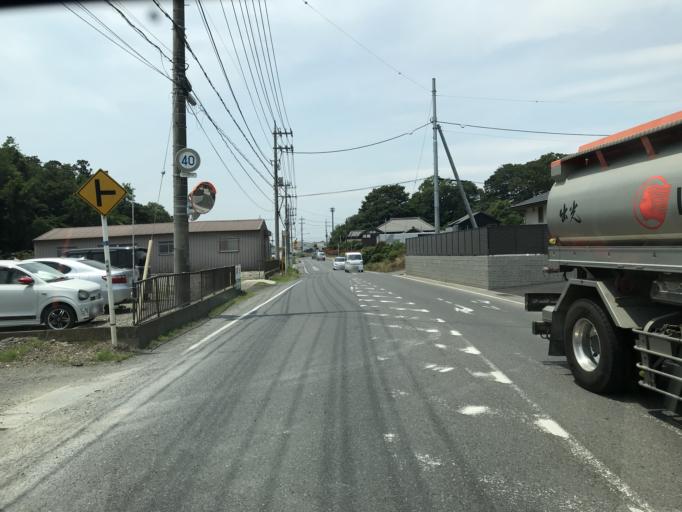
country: JP
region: Ibaraki
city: Iwai
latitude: 36.0325
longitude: 139.8357
